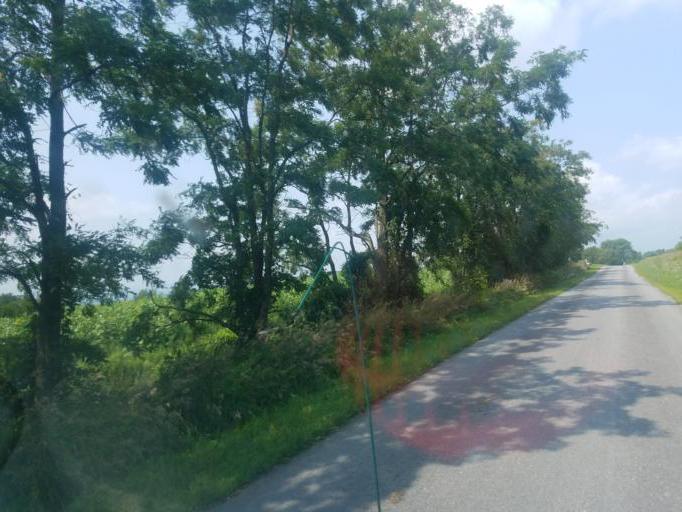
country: US
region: New York
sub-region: Montgomery County
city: Wellsville
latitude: 42.8686
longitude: -74.3272
